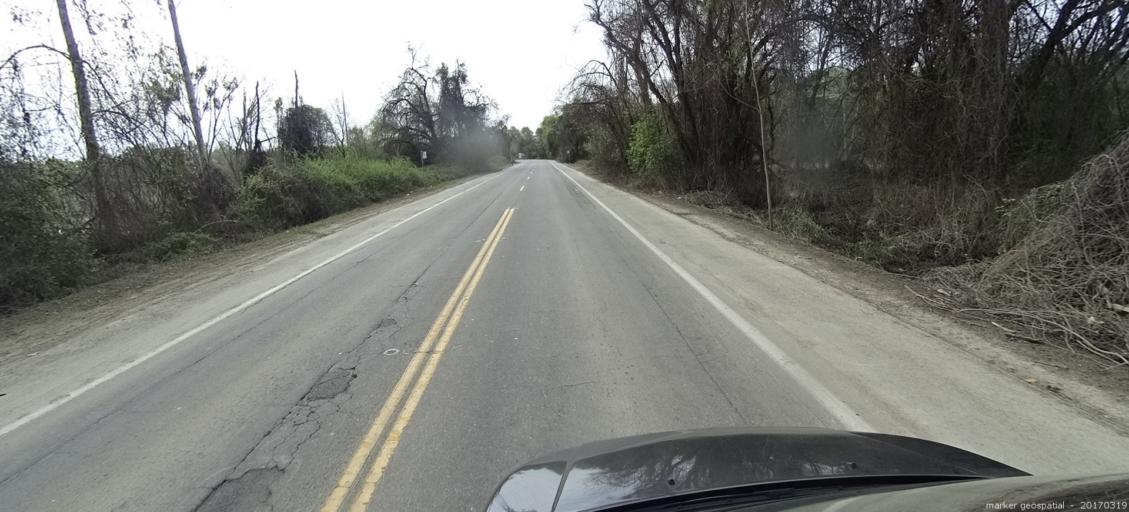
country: US
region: California
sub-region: Sacramento County
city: Sacramento
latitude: 38.6019
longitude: -121.4750
